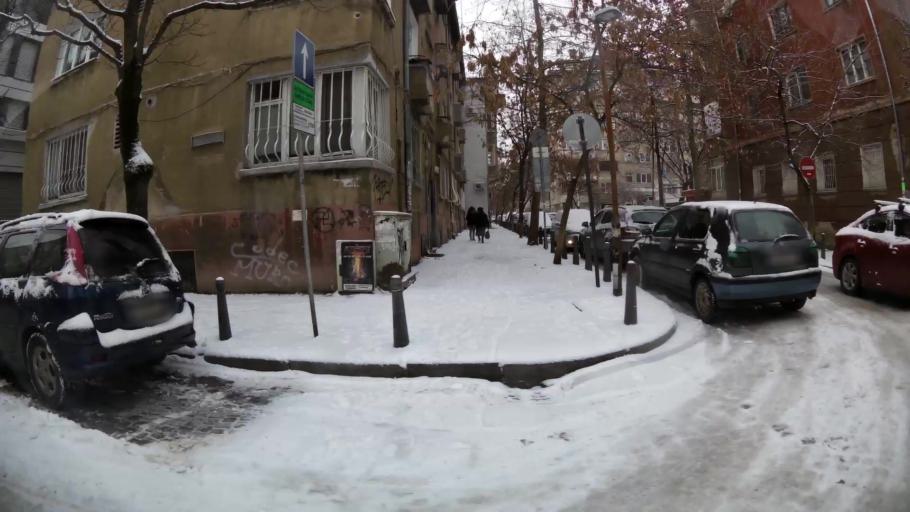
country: BG
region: Sofia-Capital
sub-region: Stolichna Obshtina
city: Sofia
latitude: 42.6903
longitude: 23.3104
